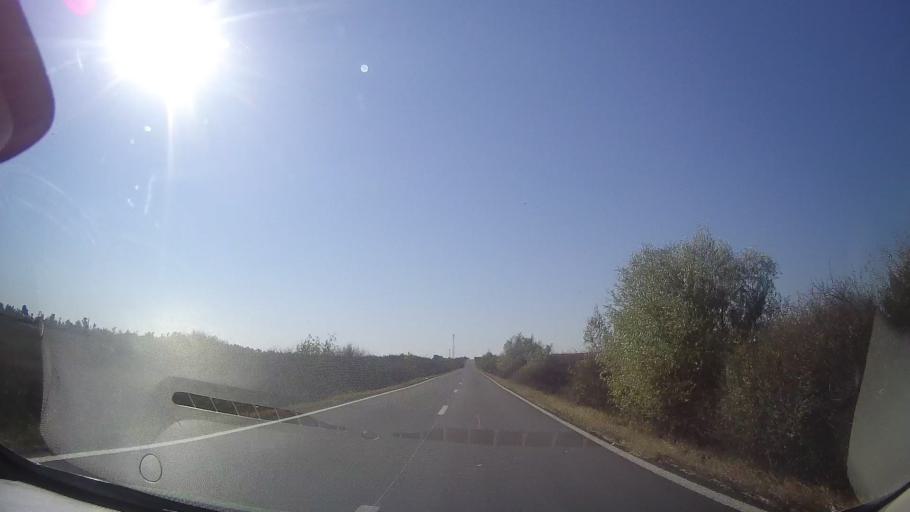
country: RO
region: Timis
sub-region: Comuna Belint
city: Belint
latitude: 45.7719
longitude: 21.7301
